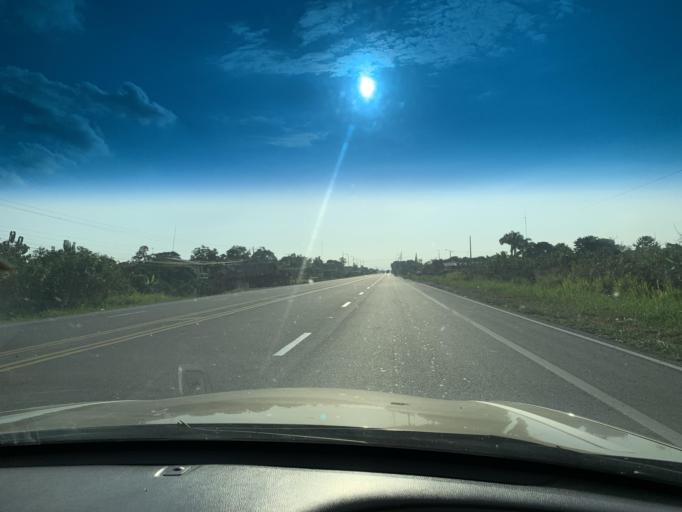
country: EC
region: Guayas
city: Naranjito
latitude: -2.2566
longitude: -79.5882
